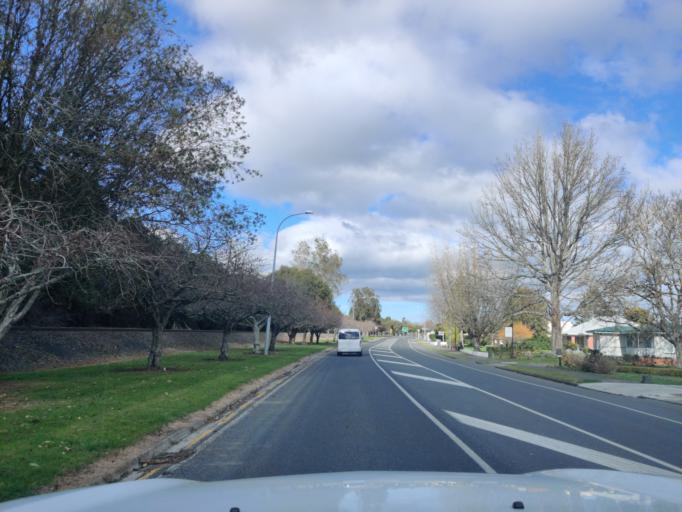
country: NZ
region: Waikato
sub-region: Matamata-Piako District
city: Matamata
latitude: -37.8214
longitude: 175.7711
